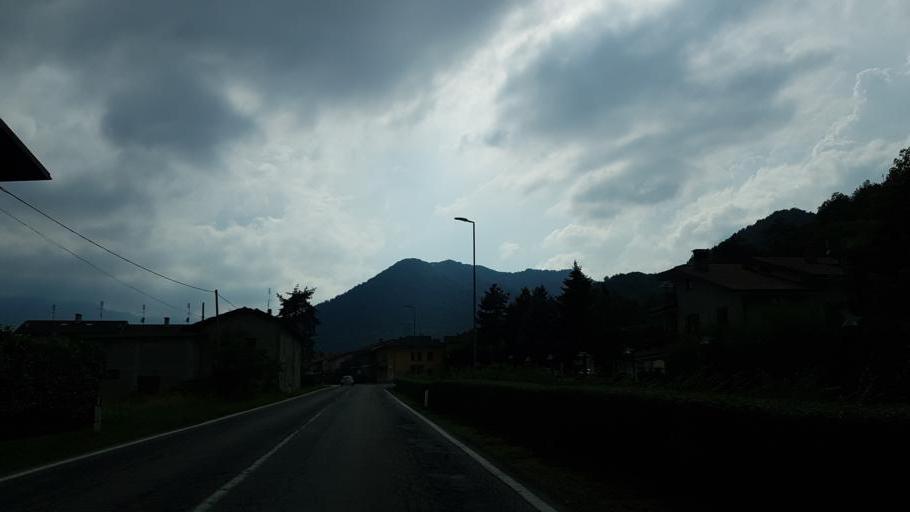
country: IT
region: Piedmont
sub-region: Provincia di Cuneo
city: Gaiola
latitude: 44.3364
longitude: 7.4114
